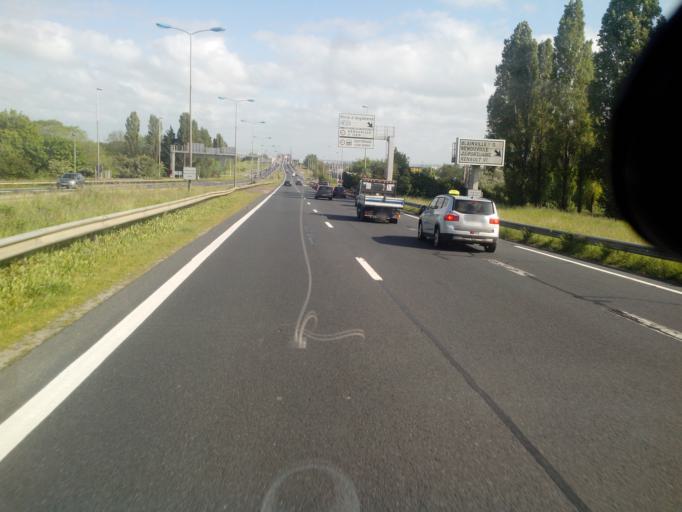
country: FR
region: Lower Normandy
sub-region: Departement du Calvados
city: Caen
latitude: 49.1939
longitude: -0.3368
